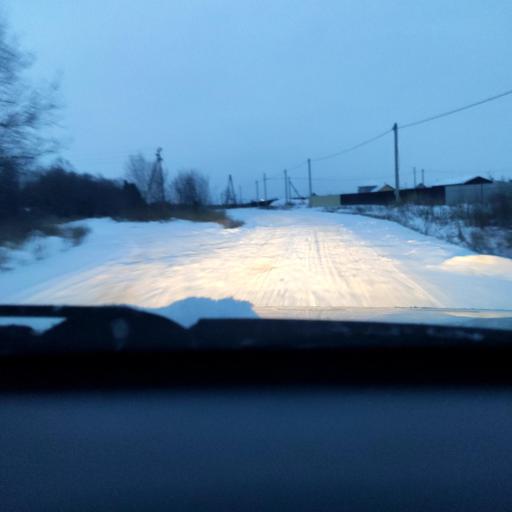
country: RU
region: Perm
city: Froly
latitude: 57.9471
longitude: 56.2299
